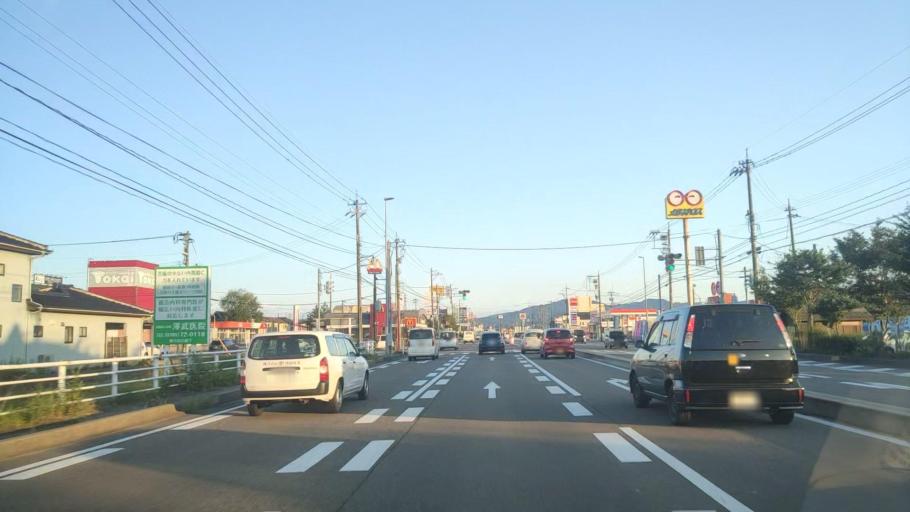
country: JP
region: Toyama
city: Himi
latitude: 36.8406
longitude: 136.9853
